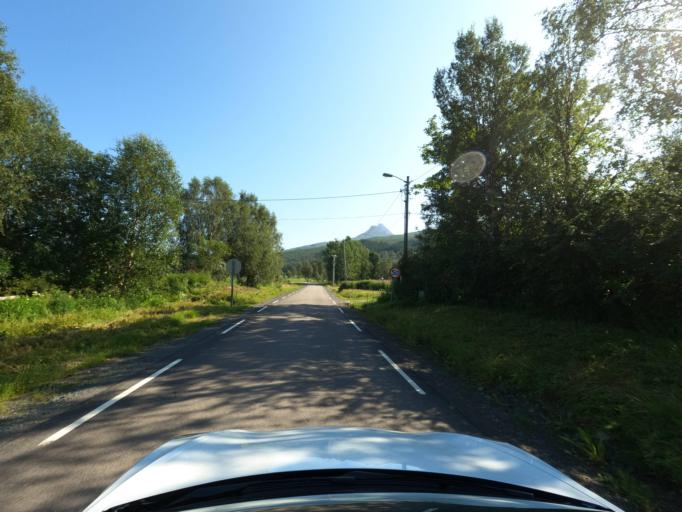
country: NO
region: Nordland
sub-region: Narvik
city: Narvik
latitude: 68.3988
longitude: 17.2951
